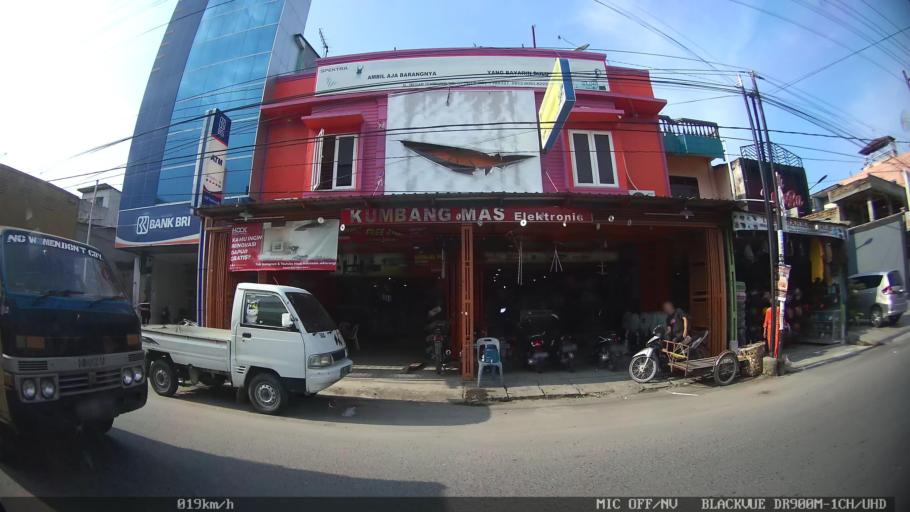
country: ID
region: North Sumatra
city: Medan
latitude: 3.5968
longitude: 98.7481
